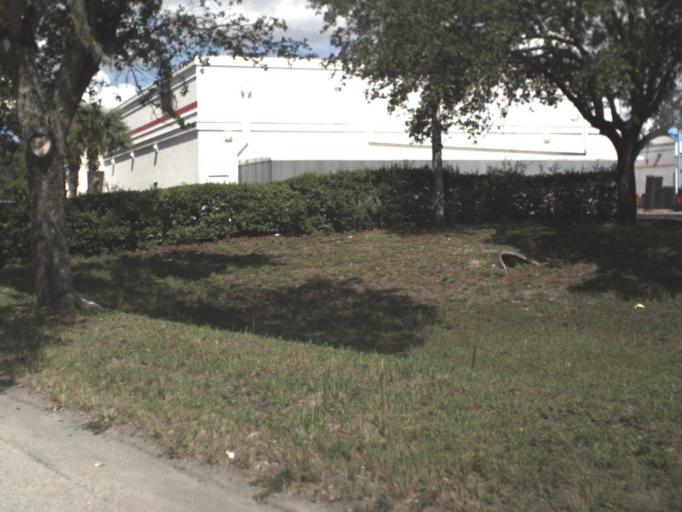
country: US
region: Florida
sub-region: Hillsborough County
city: East Lake-Orient Park
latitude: 27.9622
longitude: -82.4006
